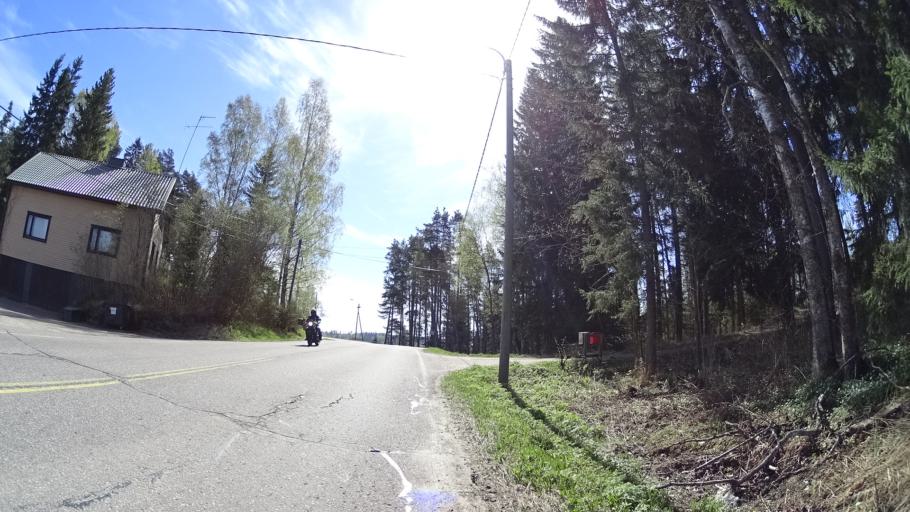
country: FI
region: Uusimaa
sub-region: Helsinki
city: Nurmijaervi
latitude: 60.3641
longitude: 24.8506
